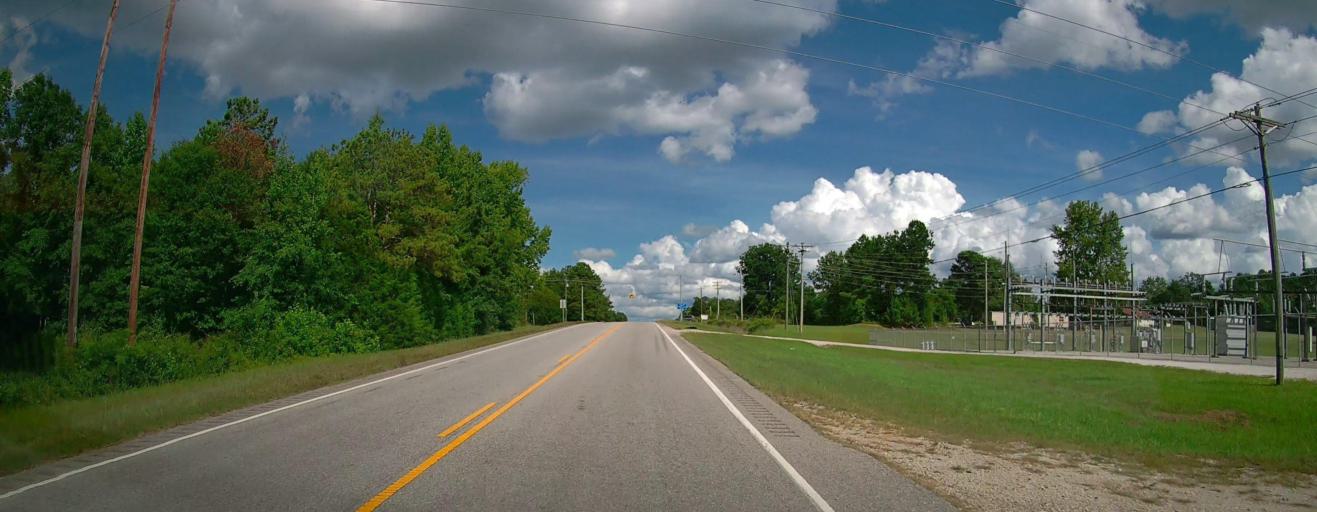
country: US
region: Alabama
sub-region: Macon County
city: Tuskegee
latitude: 32.4639
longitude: -85.5641
